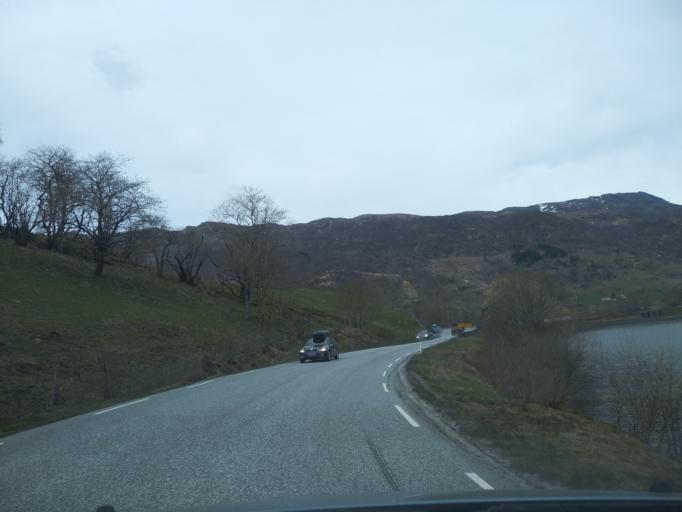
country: NO
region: Hordaland
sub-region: Etne
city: Etne
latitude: 59.6799
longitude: 6.0098
